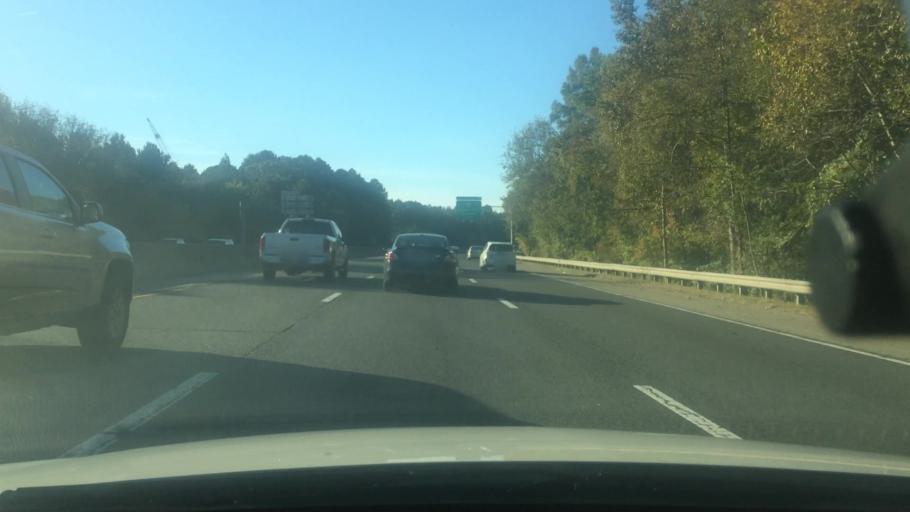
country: US
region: North Carolina
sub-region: Orange County
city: Chapel Hill
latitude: 35.9052
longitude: -78.9715
